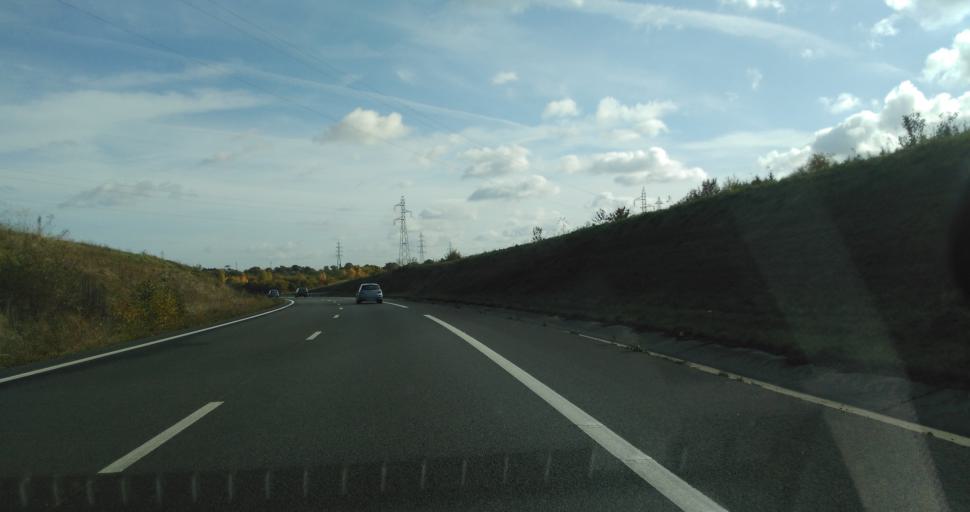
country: FR
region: Brittany
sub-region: Departement d'Ille-et-Vilaine
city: Vezin-le-Coquet
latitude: 48.1247
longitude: -1.7406
